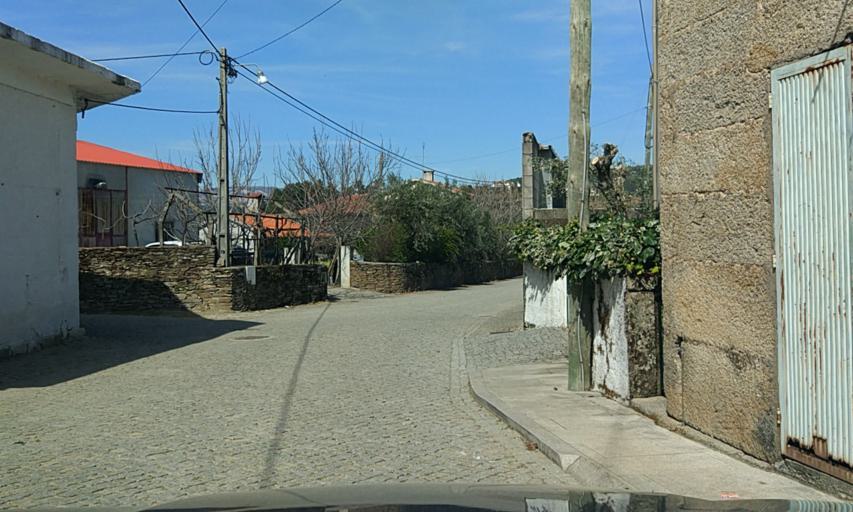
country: PT
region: Vila Real
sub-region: Sabrosa
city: Sabrosa
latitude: 41.3065
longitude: -7.5596
